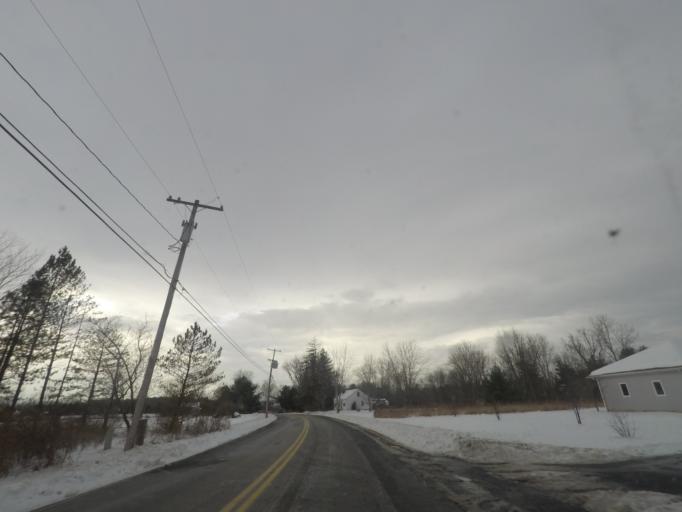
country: US
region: New York
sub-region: Rensselaer County
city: Castleton-on-Hudson
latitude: 42.5050
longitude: -73.7421
